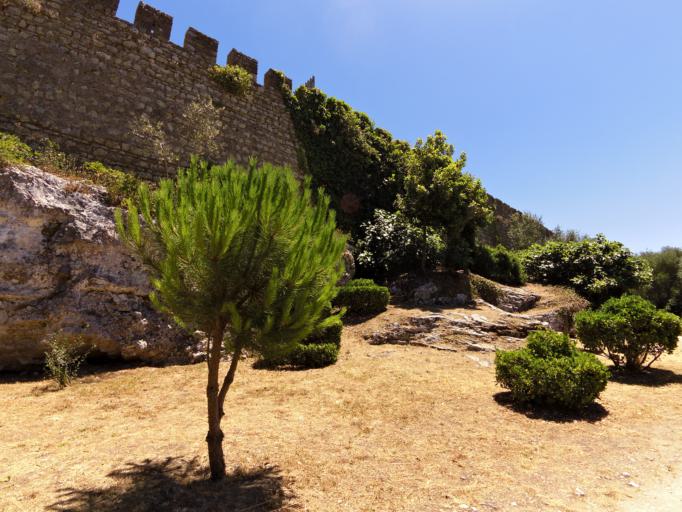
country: PT
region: Leiria
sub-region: Obidos
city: Obidos
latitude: 39.3624
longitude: -9.1577
